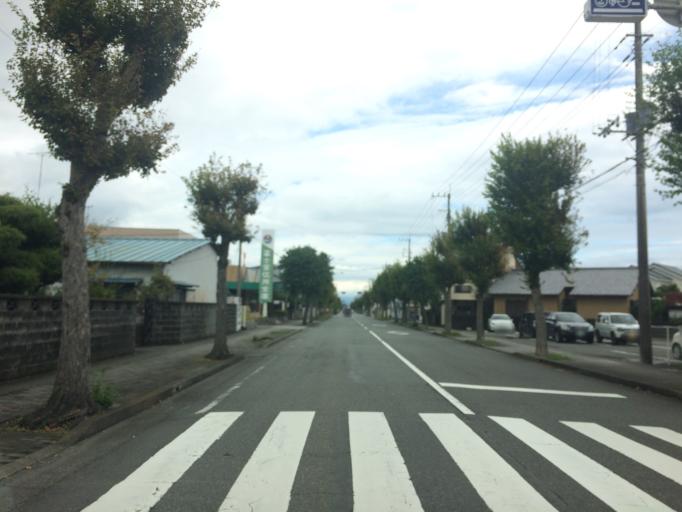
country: JP
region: Shizuoka
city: Fuji
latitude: 35.1442
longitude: 138.6554
